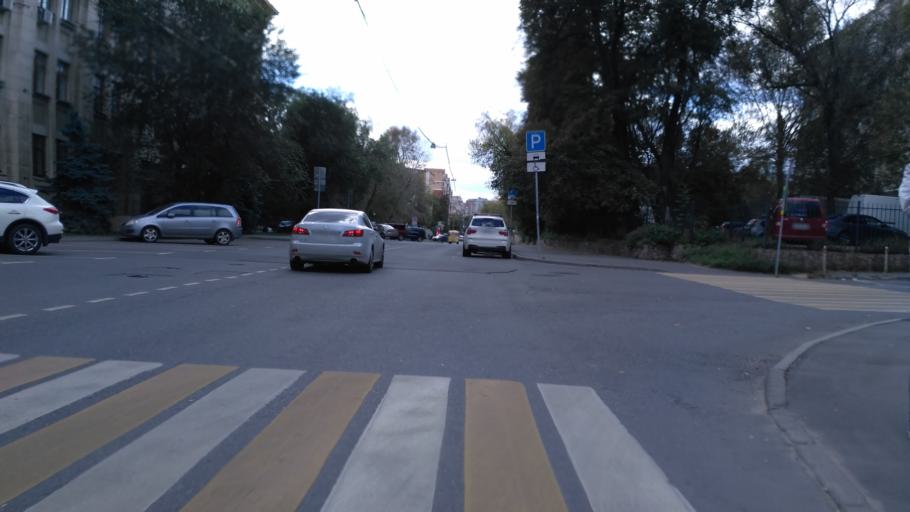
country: RU
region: Moscow
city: Lefortovo
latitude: 55.7782
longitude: 37.6964
